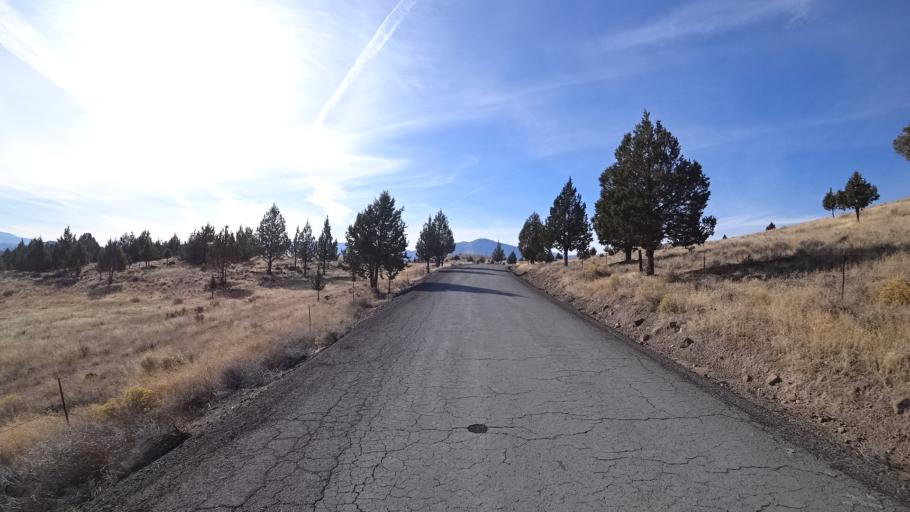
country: US
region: California
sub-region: Siskiyou County
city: Weed
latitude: 41.5558
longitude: -122.4729
